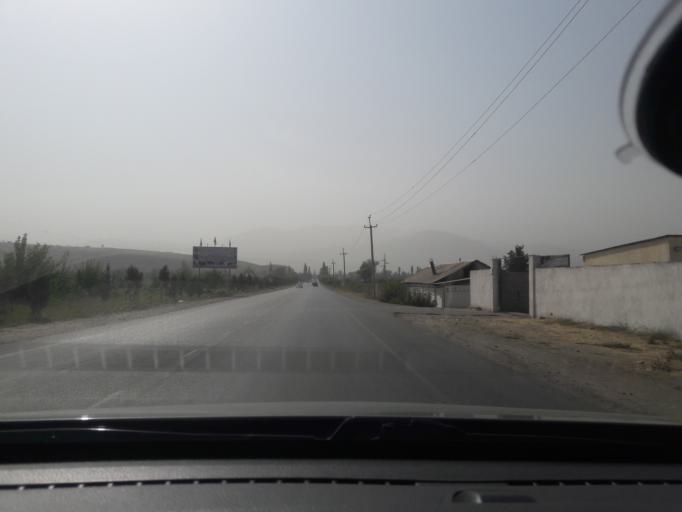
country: TJ
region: Republican Subordination
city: Vahdat
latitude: 38.5298
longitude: 69.0261
